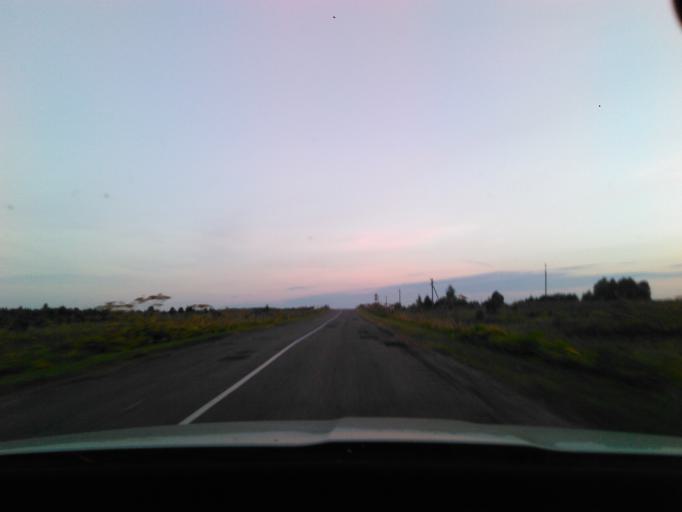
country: RU
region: Moskovskaya
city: Klin
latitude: 56.2240
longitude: 36.7404
